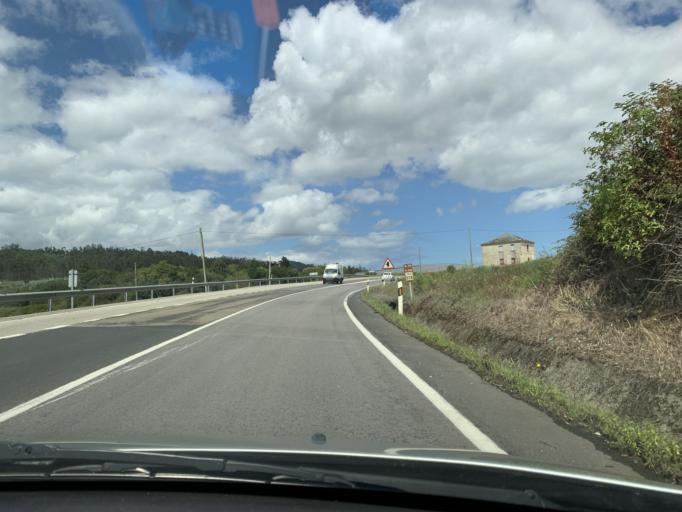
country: ES
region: Galicia
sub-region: Provincia de Lugo
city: Barreiros
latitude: 43.4844
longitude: -7.2913
